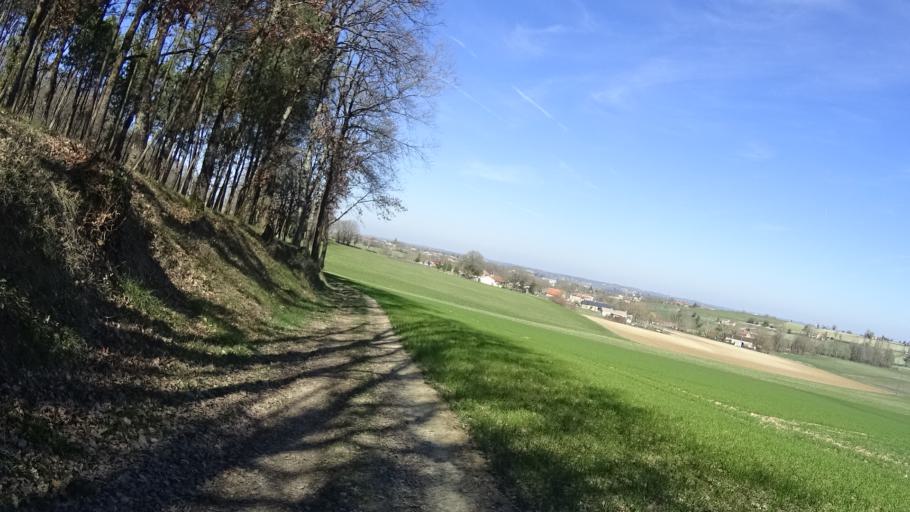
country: FR
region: Aquitaine
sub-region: Departement de la Dordogne
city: Riberac
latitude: 45.2180
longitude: 0.3322
